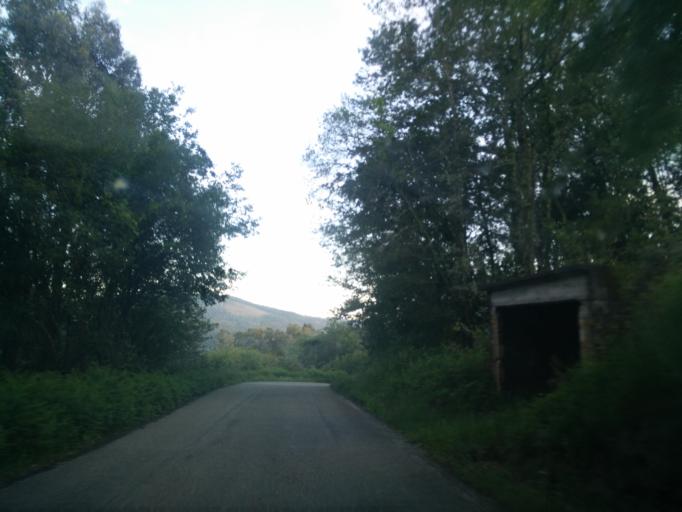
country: ES
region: Galicia
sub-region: Provincia de Pontevedra
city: Mondariz
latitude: 42.2546
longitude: -8.4226
